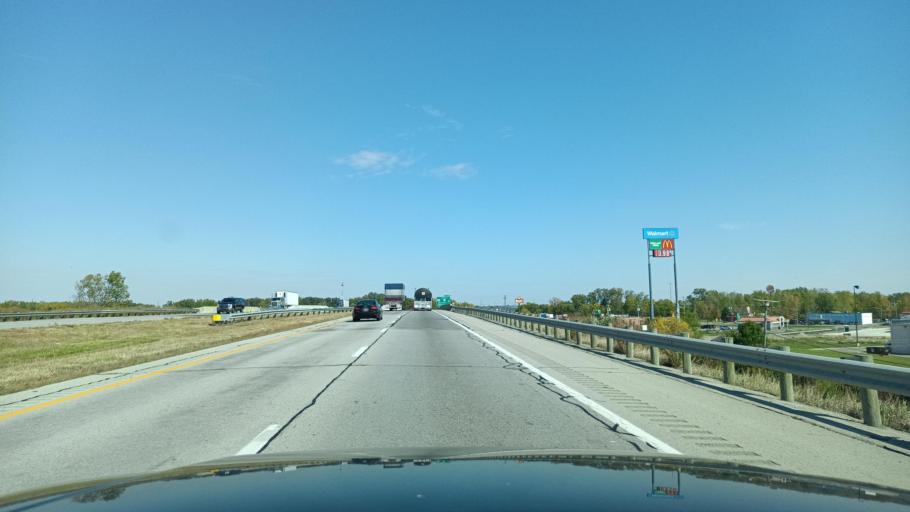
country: US
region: Ohio
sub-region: Henry County
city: Napoleon
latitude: 41.4051
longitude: -84.1363
